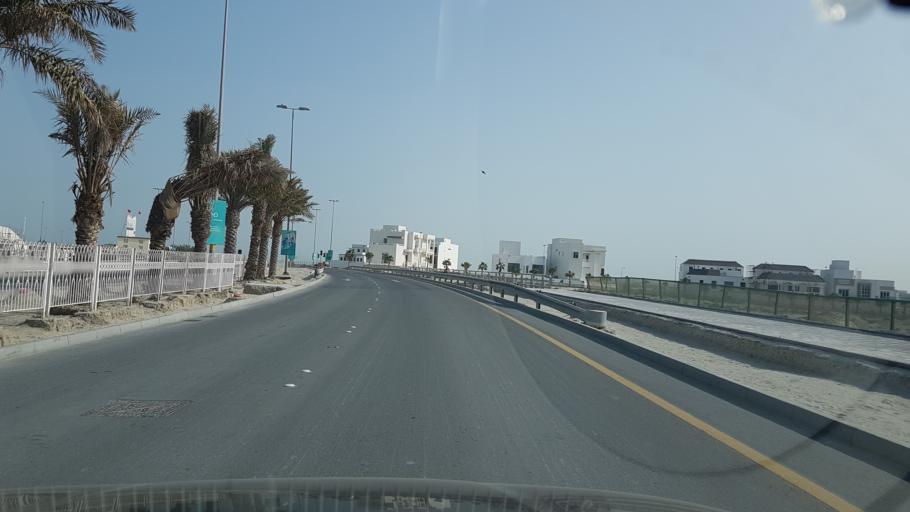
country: BH
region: Muharraq
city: Al Hadd
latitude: 26.2701
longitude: 50.6700
